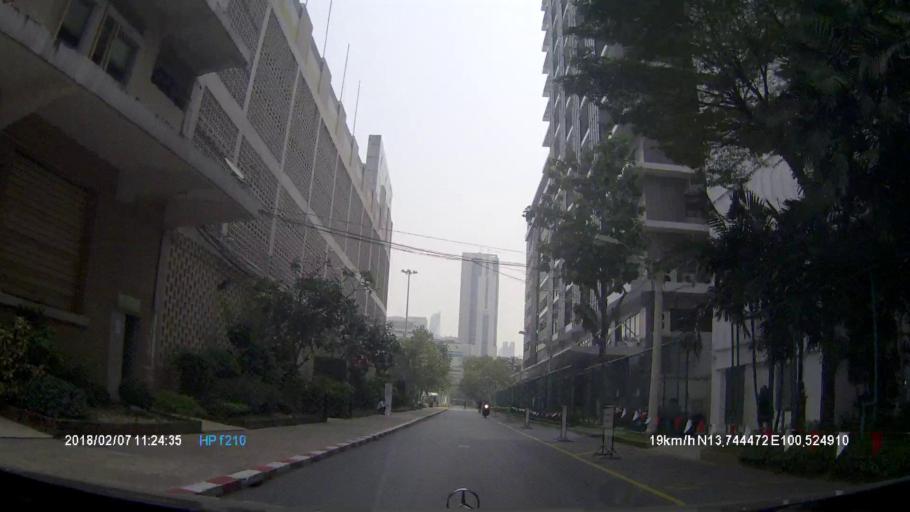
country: TH
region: Bangkok
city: Pathum Wan
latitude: 13.7444
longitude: 100.5252
